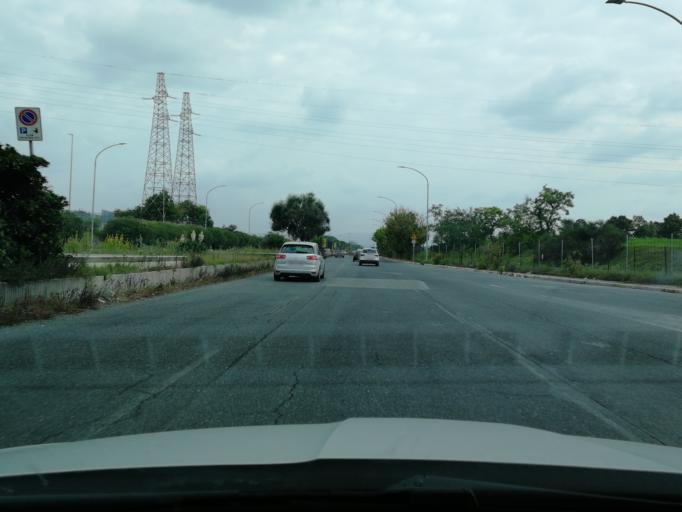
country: IT
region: Latium
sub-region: Citta metropolitana di Roma Capitale
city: Ciampino
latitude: 41.8483
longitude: 12.5757
